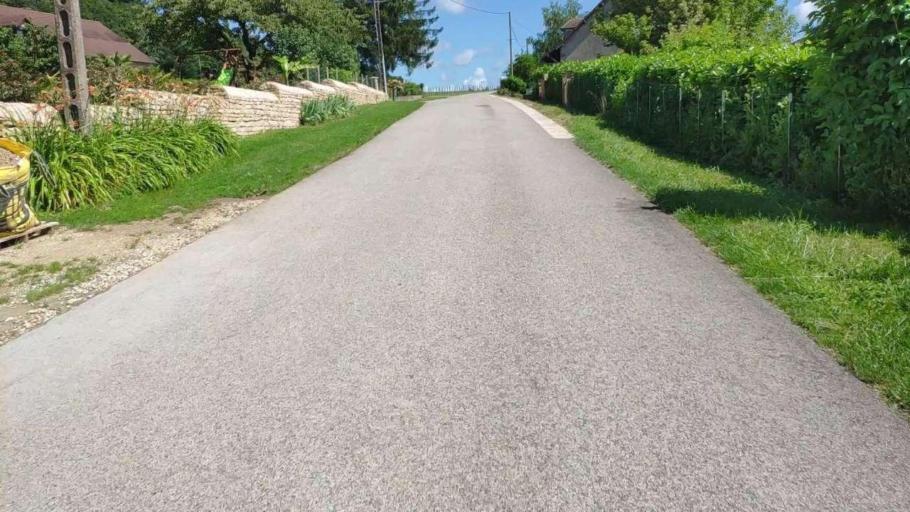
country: FR
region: Franche-Comte
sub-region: Departement du Jura
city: Bletterans
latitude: 46.8033
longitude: 5.5624
